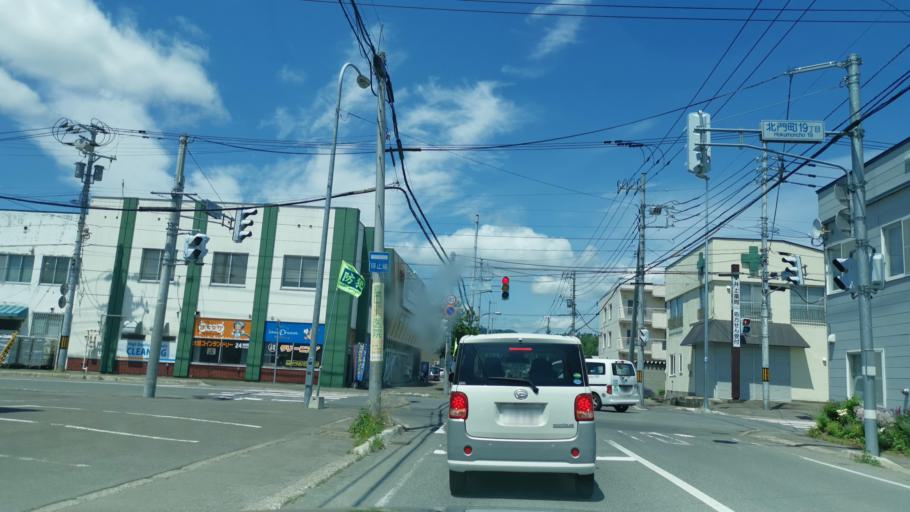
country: JP
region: Hokkaido
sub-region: Asahikawa-shi
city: Asahikawa
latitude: 43.7935
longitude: 142.3338
